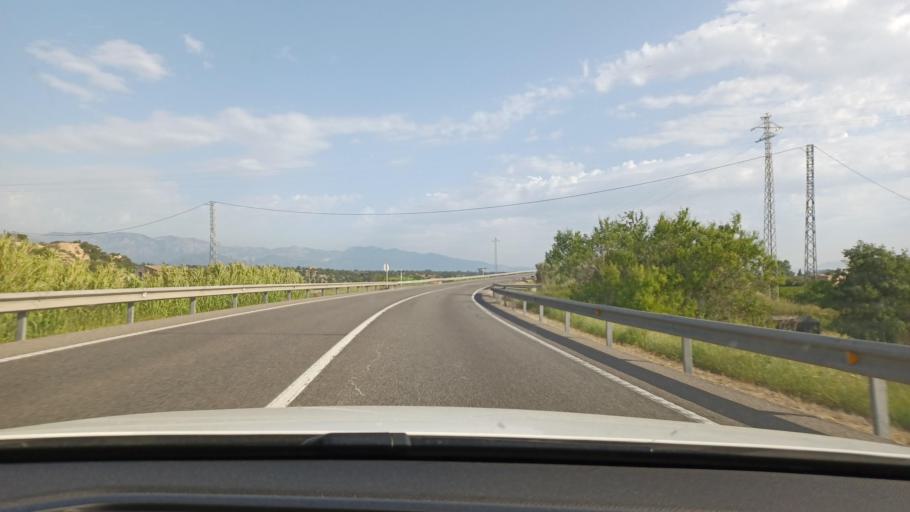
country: ES
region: Catalonia
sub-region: Provincia de Tarragona
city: Tortosa
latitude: 40.7884
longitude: 0.4966
